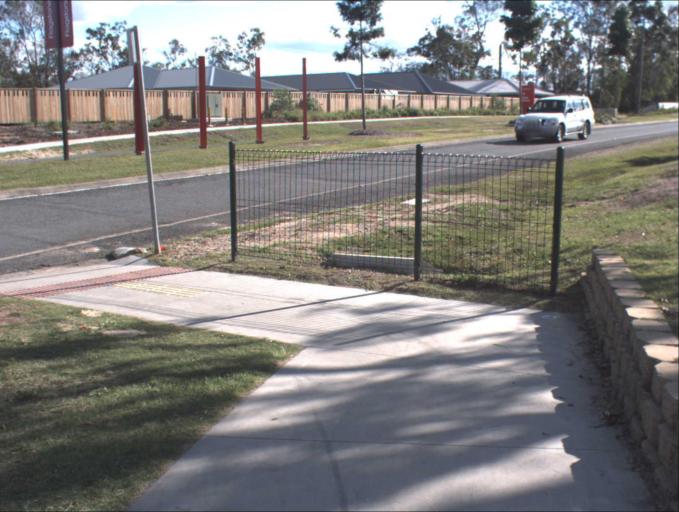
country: AU
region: Queensland
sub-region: Logan
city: North Maclean
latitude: -27.8090
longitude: 152.9556
